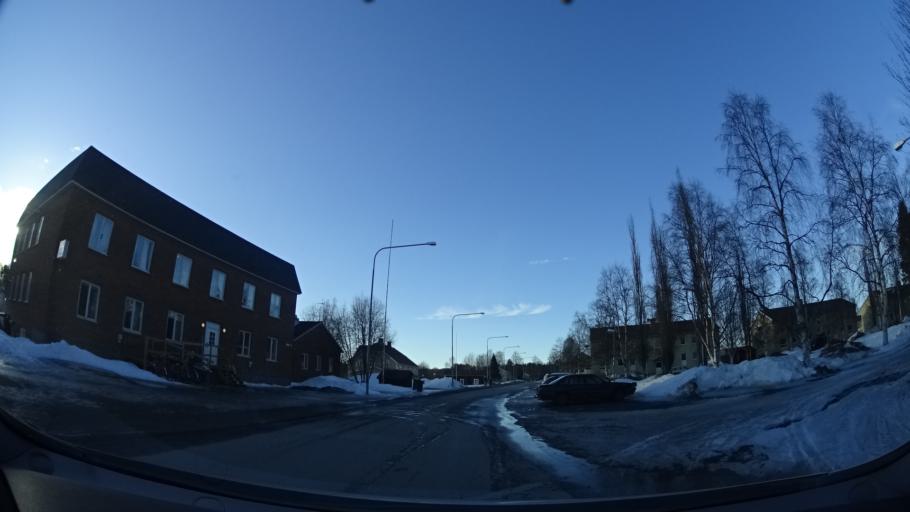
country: SE
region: Vaesterbotten
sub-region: Skelleftea Kommun
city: Byske
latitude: 64.9509
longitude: 21.2047
